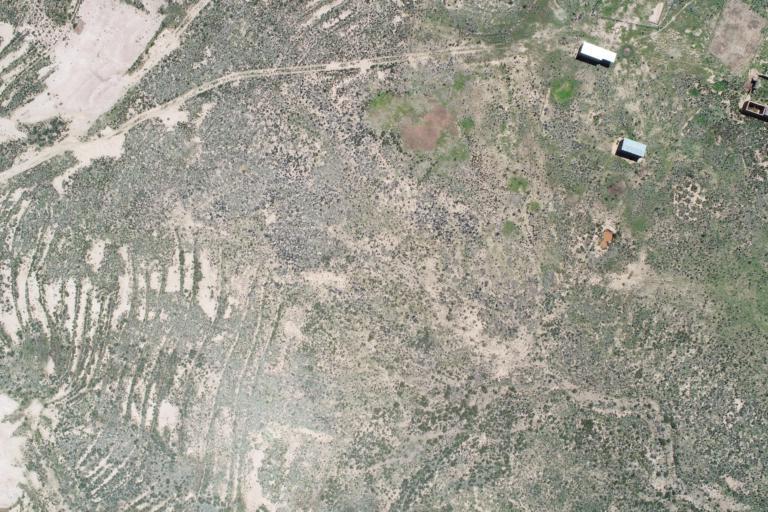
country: BO
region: La Paz
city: Curahuara de Carangas
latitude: -17.3184
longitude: -68.4950
